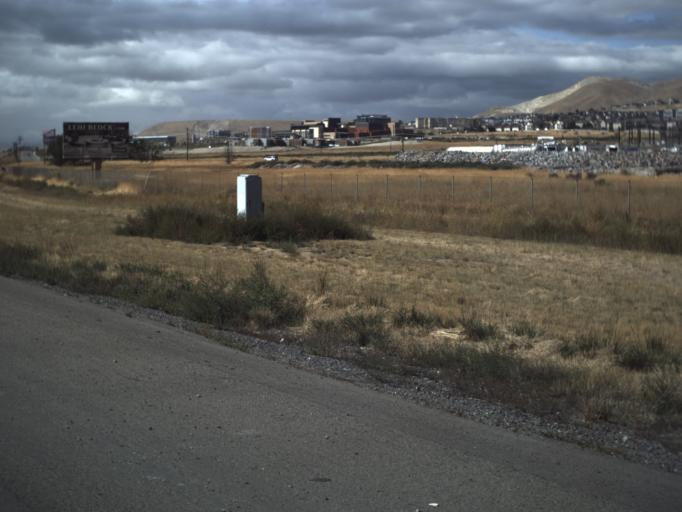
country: US
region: Utah
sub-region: Utah County
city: Lehi
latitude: 40.4155
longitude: -111.8713
